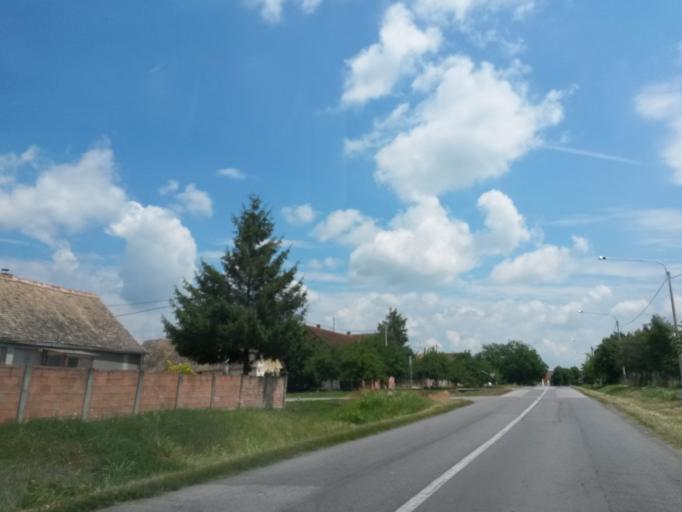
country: HR
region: Osjecko-Baranjska
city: Sarvas
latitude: 45.5190
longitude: 18.8619
